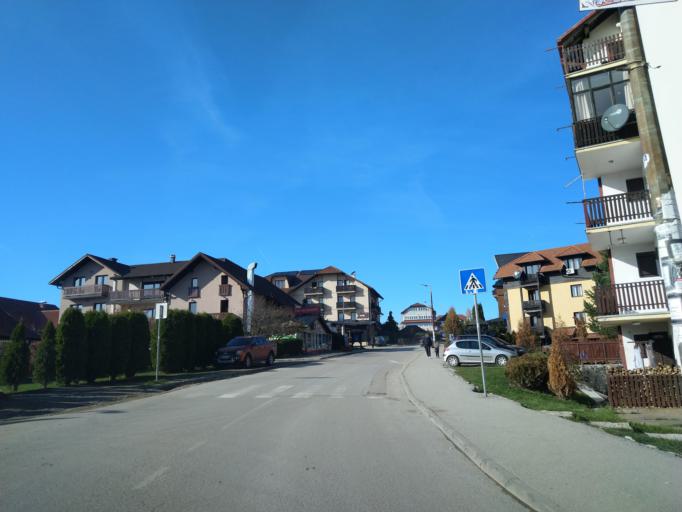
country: RS
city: Zlatibor
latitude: 43.7255
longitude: 19.6923
